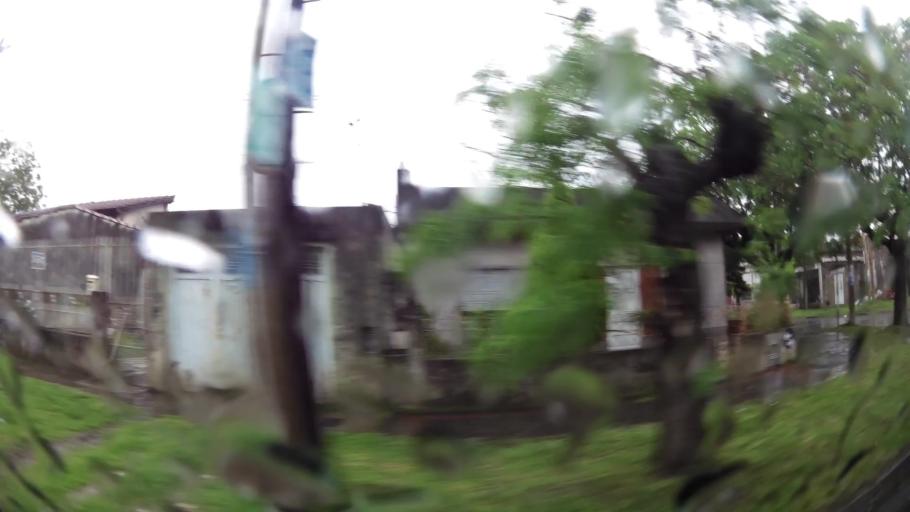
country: AR
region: Buenos Aires
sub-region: Partido de Lanus
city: Lanus
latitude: -34.7128
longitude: -58.4121
